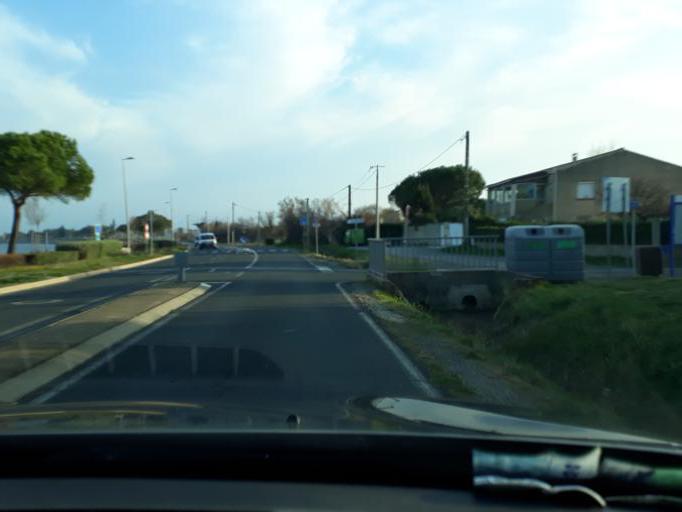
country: FR
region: Languedoc-Roussillon
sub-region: Departement de l'Herault
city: Marseillan
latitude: 43.3451
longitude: 3.5315
